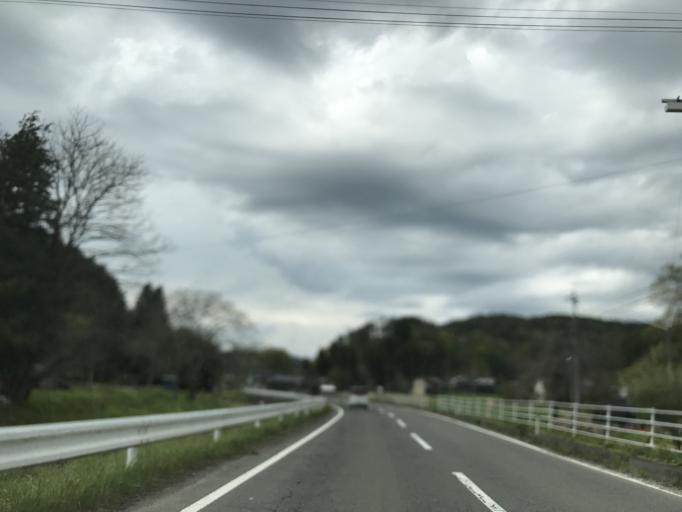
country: JP
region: Iwate
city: Ichinoseki
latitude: 38.7804
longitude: 141.3284
